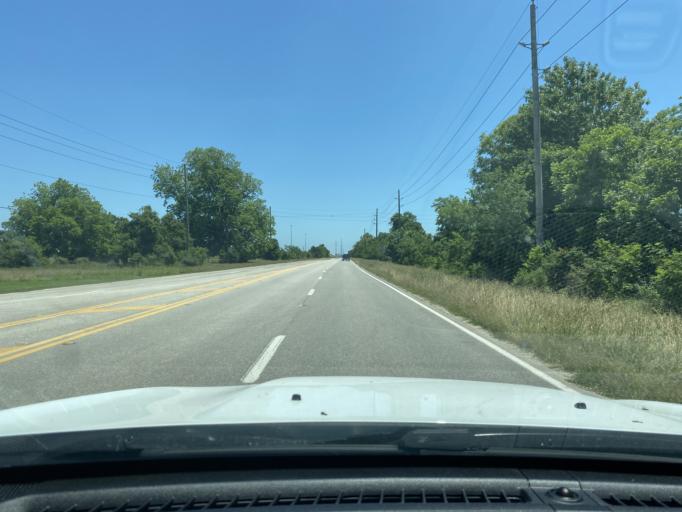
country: US
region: Texas
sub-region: Waller County
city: Waller
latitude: 30.0262
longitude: -95.8427
